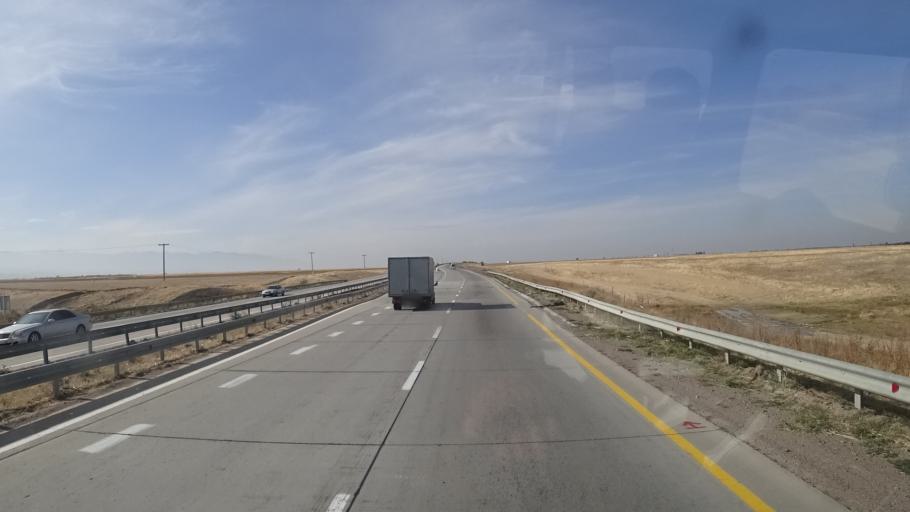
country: KZ
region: Zhambyl
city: Merke
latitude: 42.8898
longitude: 72.9811
